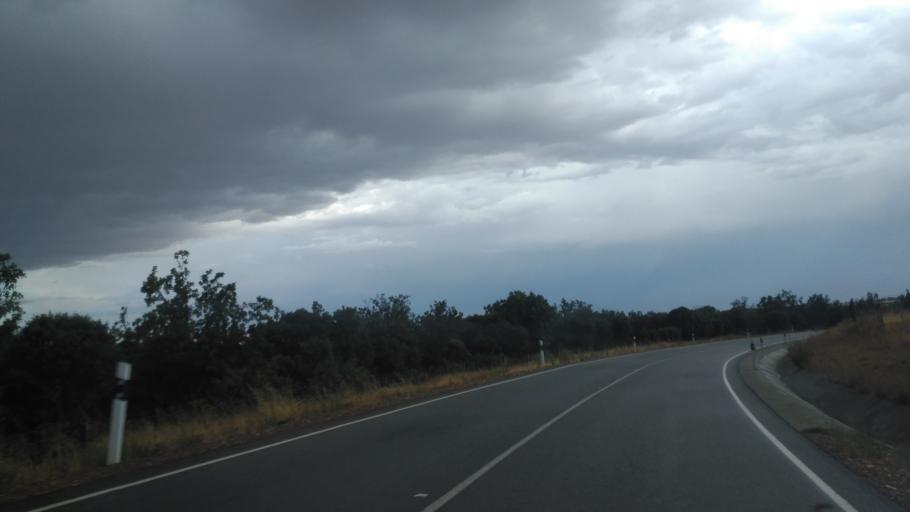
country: ES
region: Castille and Leon
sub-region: Provincia de Salamanca
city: Puebla de Yeltes
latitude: 40.6215
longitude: -6.1428
